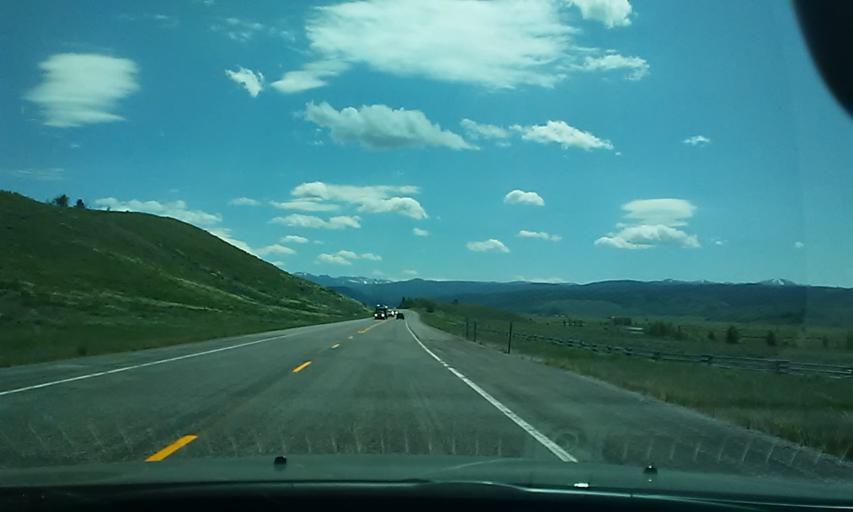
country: US
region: Wyoming
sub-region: Teton County
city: Jackson
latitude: 43.8397
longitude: -110.4526
